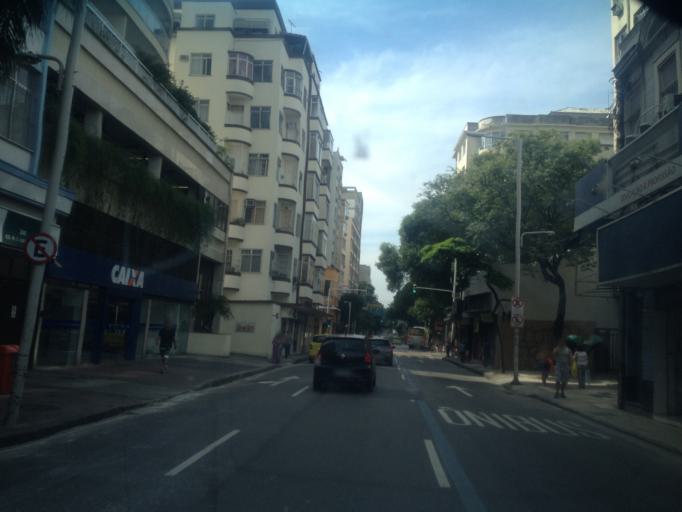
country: BR
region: Rio de Janeiro
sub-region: Rio De Janeiro
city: Rio de Janeiro
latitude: -22.9536
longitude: -43.1904
